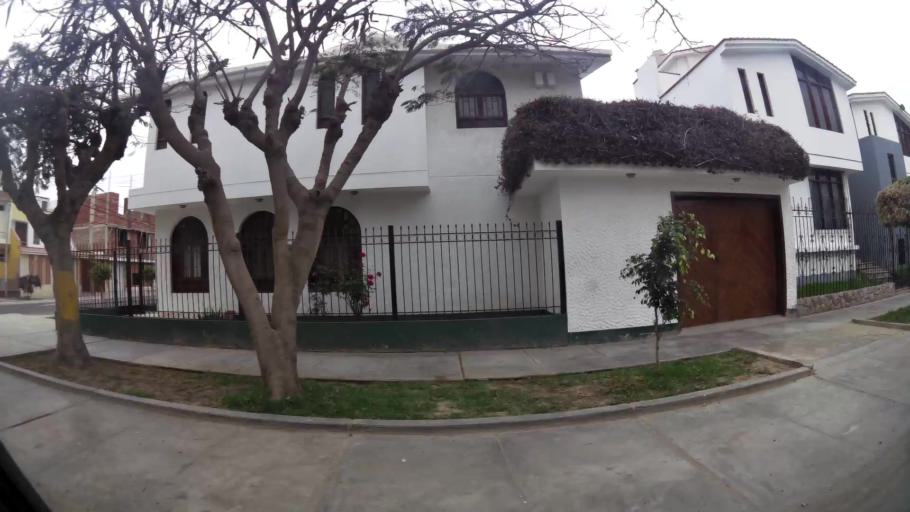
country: PE
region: La Libertad
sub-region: Provincia de Trujillo
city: Trujillo
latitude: -8.1213
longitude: -79.0379
